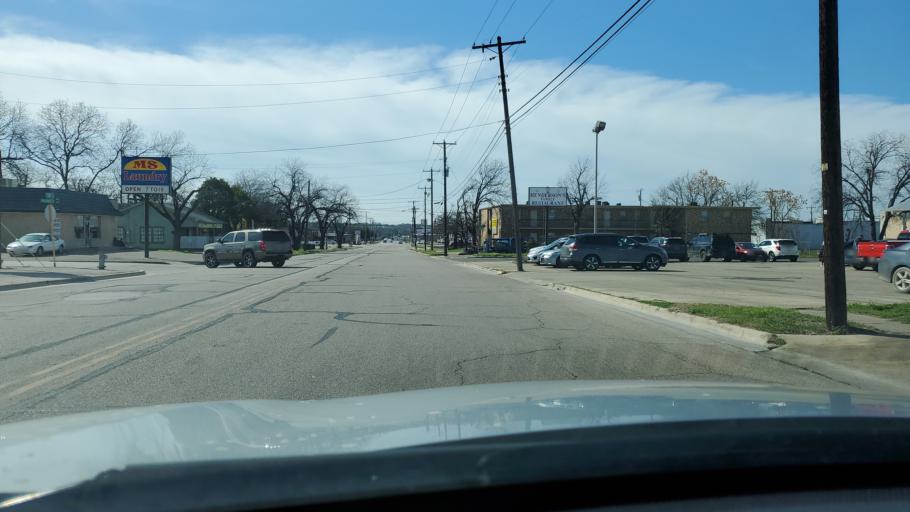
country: US
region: Texas
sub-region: Bell County
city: Killeen
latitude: 31.1227
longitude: -97.7244
